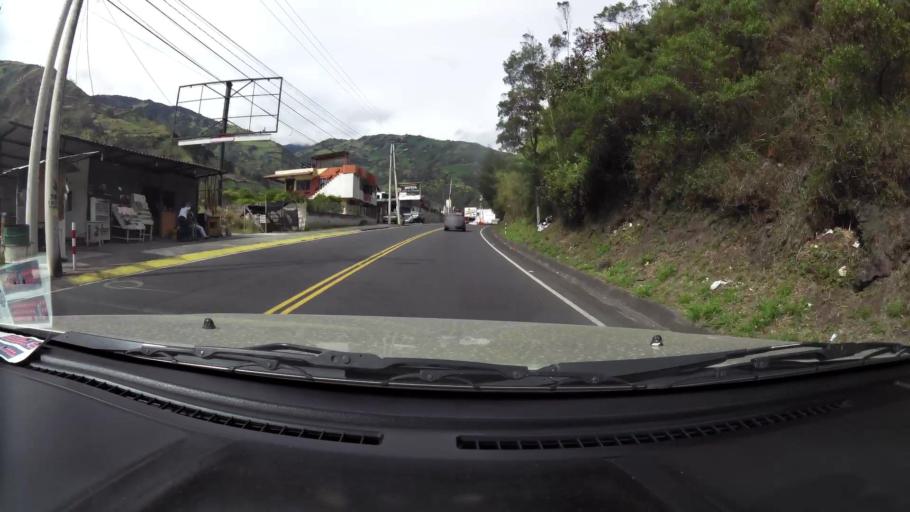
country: EC
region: Tungurahua
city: Banos
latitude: -1.4023
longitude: -78.4507
